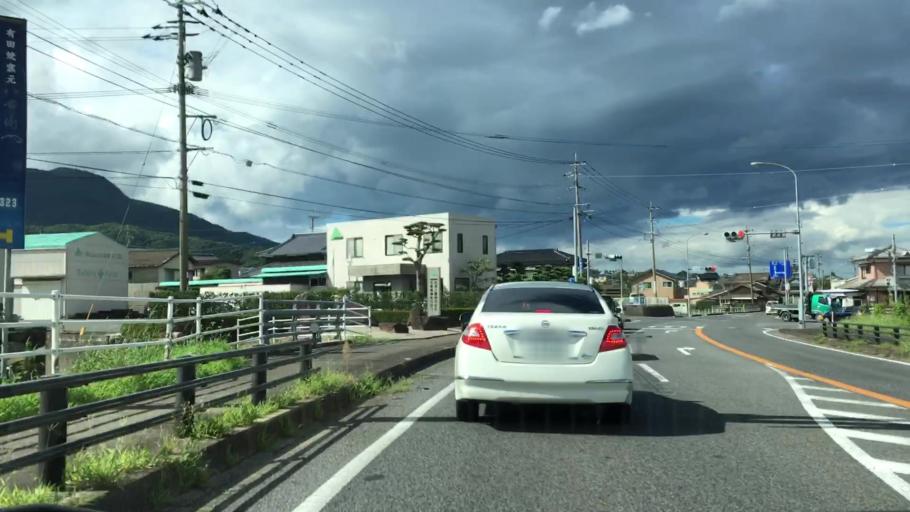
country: JP
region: Saga Prefecture
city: Imaricho-ko
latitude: 33.2248
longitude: 129.8471
